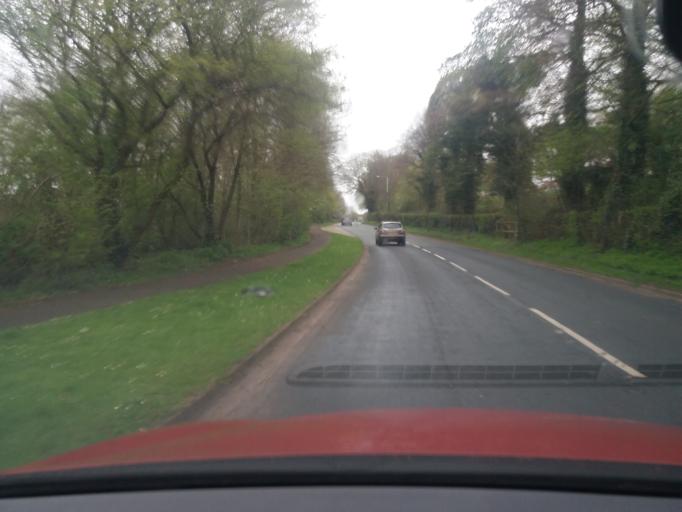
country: GB
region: England
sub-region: Lancashire
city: Clayton-le-Woods
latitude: 53.6984
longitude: -2.6341
